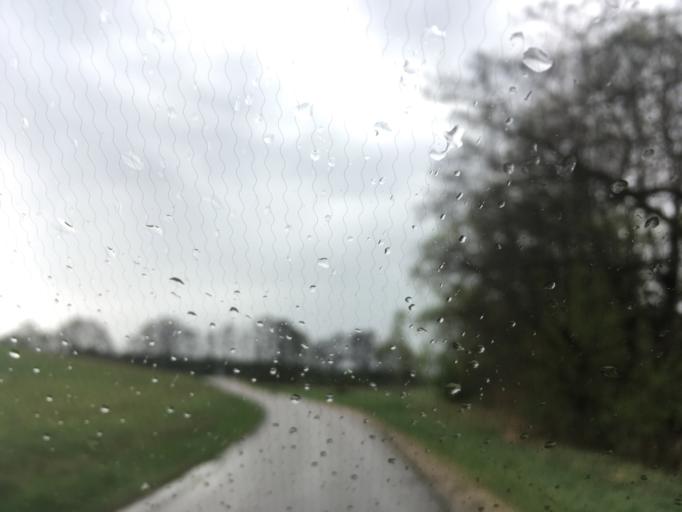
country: PL
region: Warmian-Masurian Voivodeship
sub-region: Powiat dzialdowski
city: Rybno
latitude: 53.3805
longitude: 19.9905
